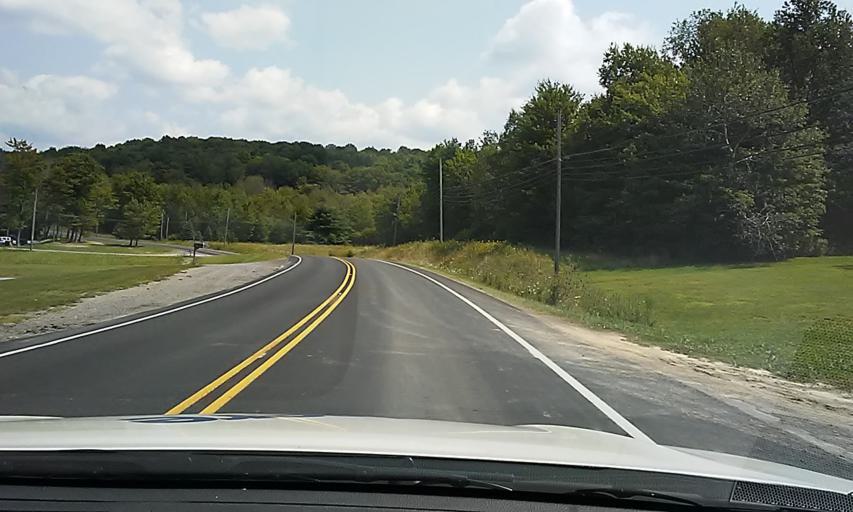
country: US
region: Pennsylvania
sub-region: Elk County
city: Saint Marys
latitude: 41.4313
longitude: -78.5154
